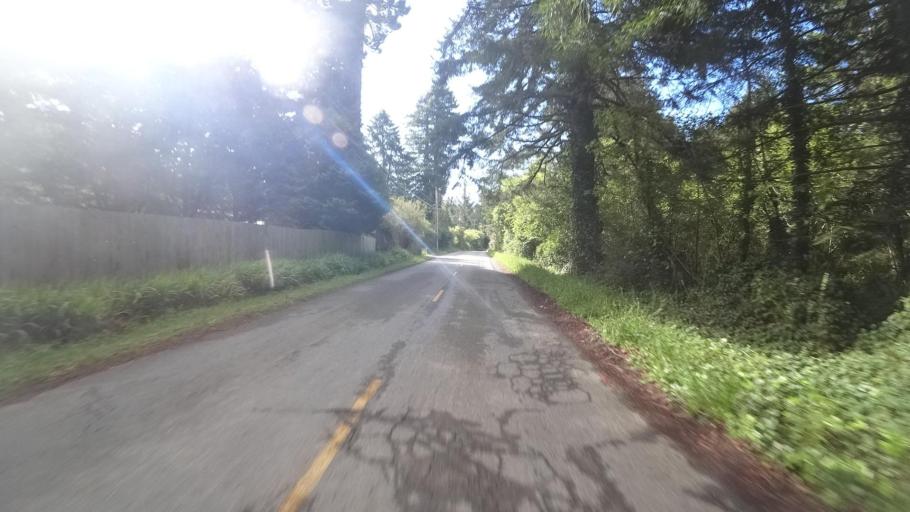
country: US
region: California
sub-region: Humboldt County
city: Westhaven-Moonstone
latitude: 41.0429
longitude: -124.1118
